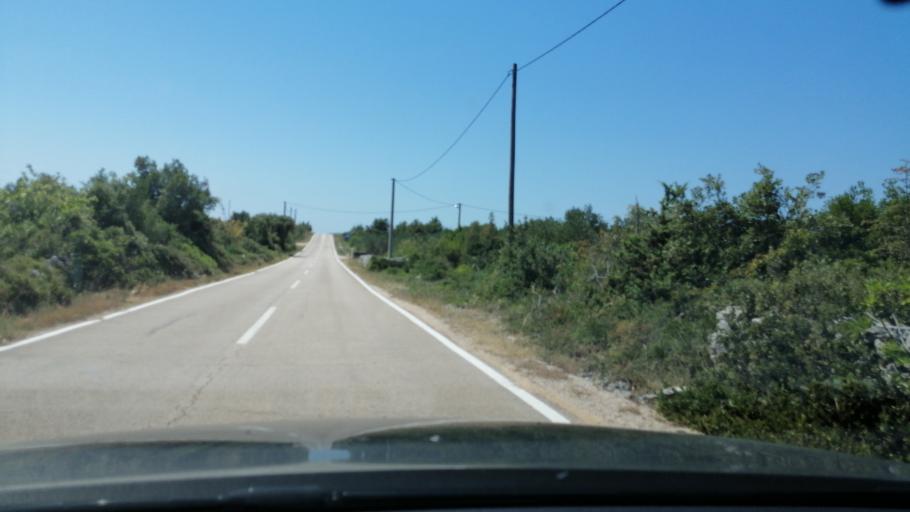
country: HR
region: Sibensko-Kniniska
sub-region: Grad Sibenik
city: Pirovac
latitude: 43.8348
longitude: 15.6864
